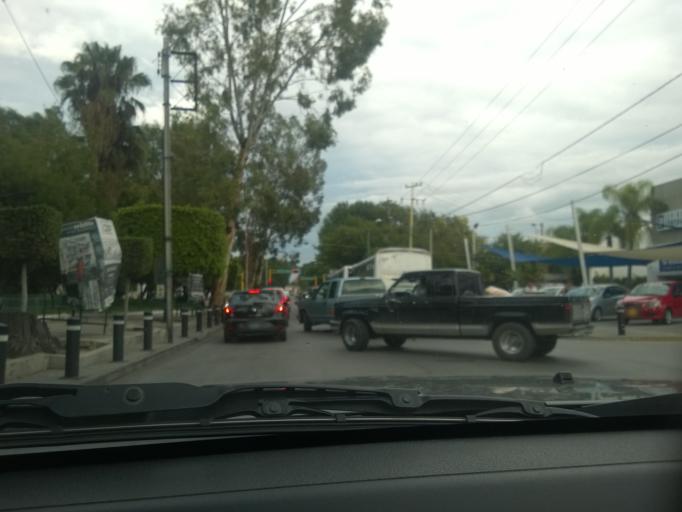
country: MX
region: Guanajuato
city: Leon
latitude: 21.1314
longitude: -101.6892
